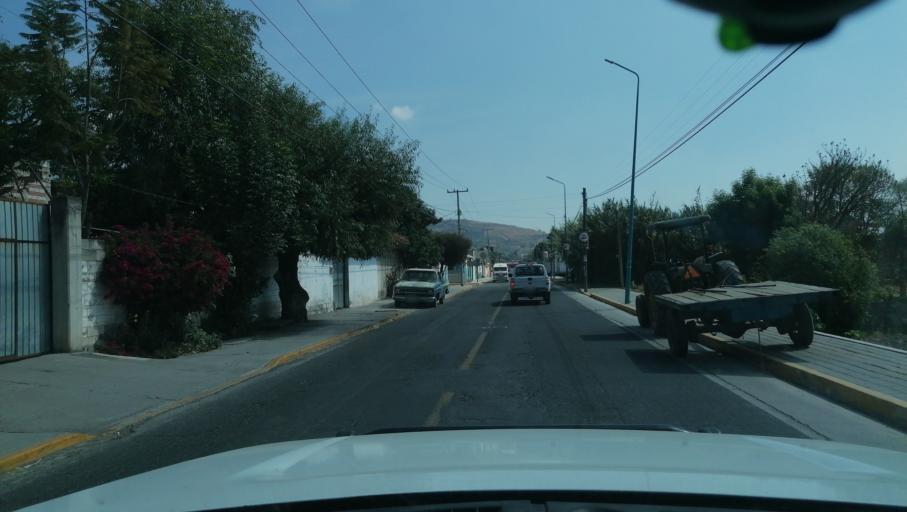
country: MX
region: Tlaxcala
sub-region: San Jeronimo Zacualpan
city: San Jeronimo Zacualpan
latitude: 19.2402
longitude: -98.2675
